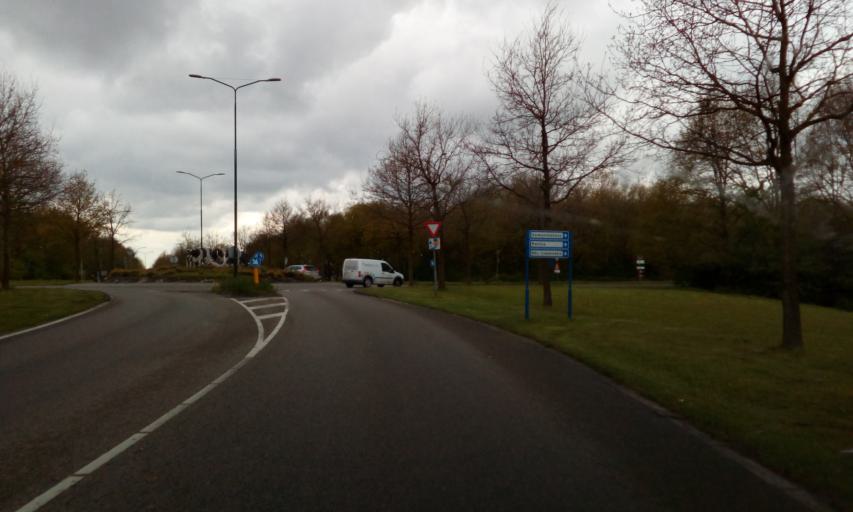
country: NL
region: North Holland
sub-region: Gemeente Blaricum
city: Blaricum
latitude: 52.2525
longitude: 5.2517
